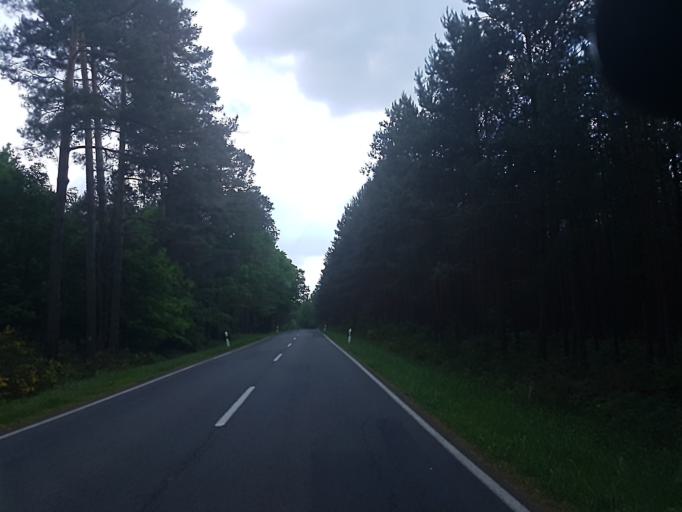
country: DE
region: Brandenburg
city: Gorzke
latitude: 52.0881
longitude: 12.3311
